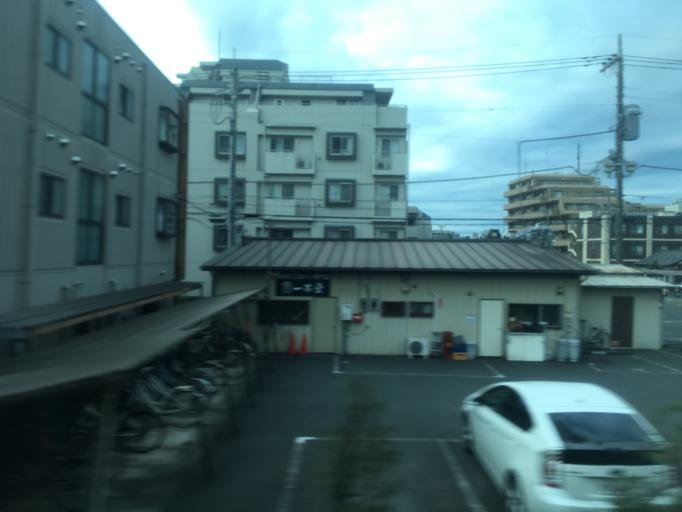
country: JP
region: Saitama
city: Okegawa
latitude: 36.0302
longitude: 139.5347
